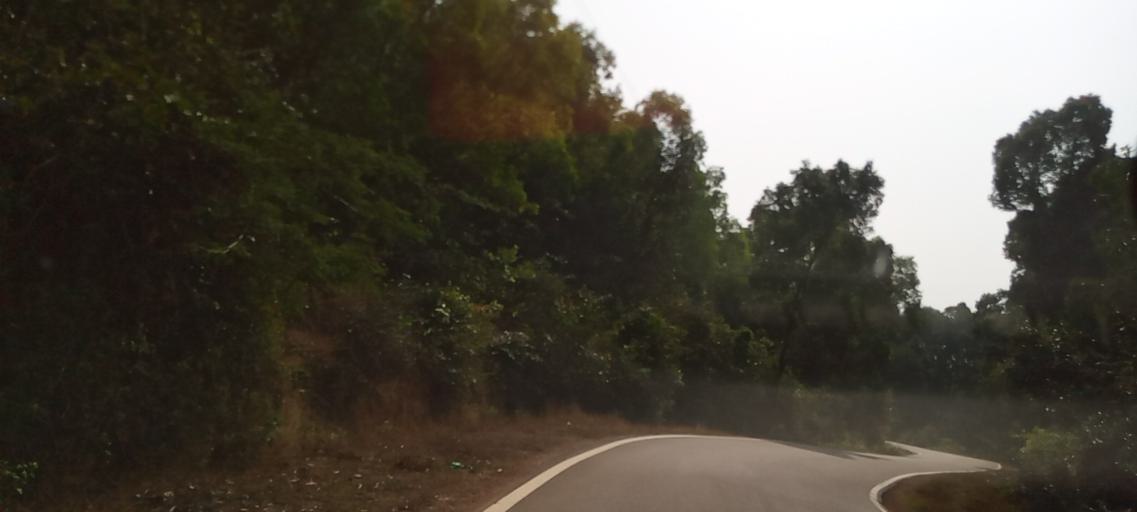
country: IN
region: Karnataka
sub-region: Udupi
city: Hosangadi
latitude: 13.5420
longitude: 74.9038
